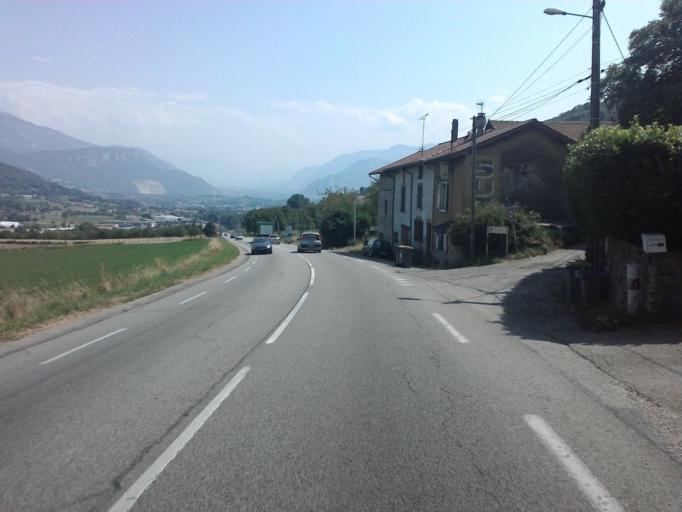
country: FR
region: Rhone-Alpes
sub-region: Departement de l'Isere
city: Chirens
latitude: 45.3944
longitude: 5.5699
